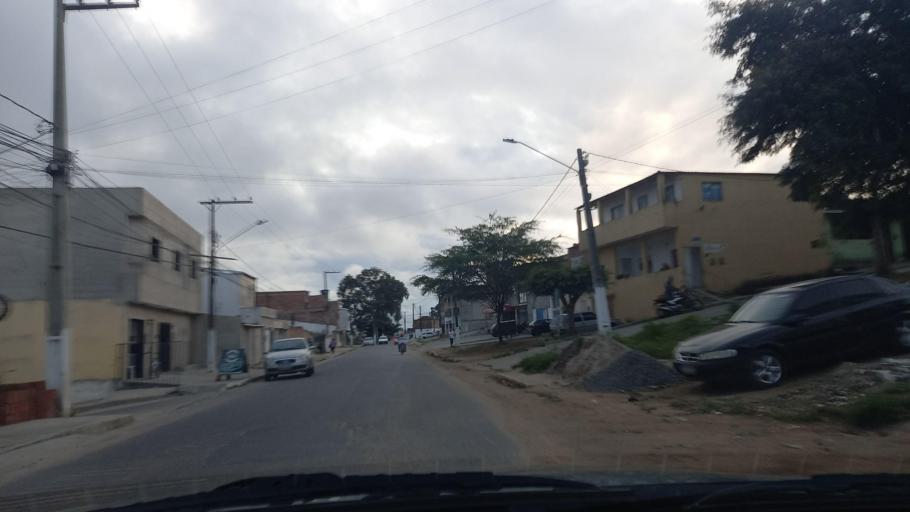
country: BR
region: Pernambuco
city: Garanhuns
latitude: -8.8895
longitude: -36.4580
